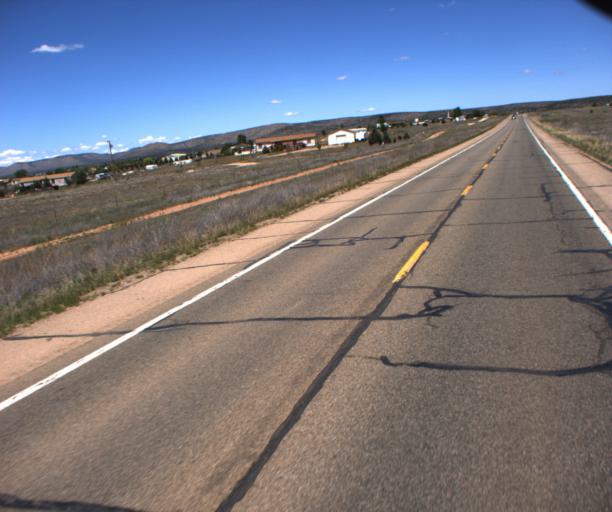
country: US
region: Arizona
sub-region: Yavapai County
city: Paulden
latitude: 34.9012
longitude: -112.4643
